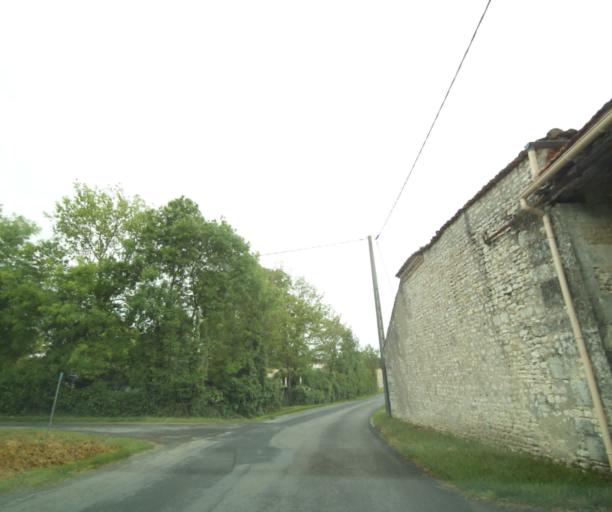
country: FR
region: Poitou-Charentes
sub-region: Departement de la Charente-Maritime
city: Chaniers
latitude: 45.6931
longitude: -0.5065
